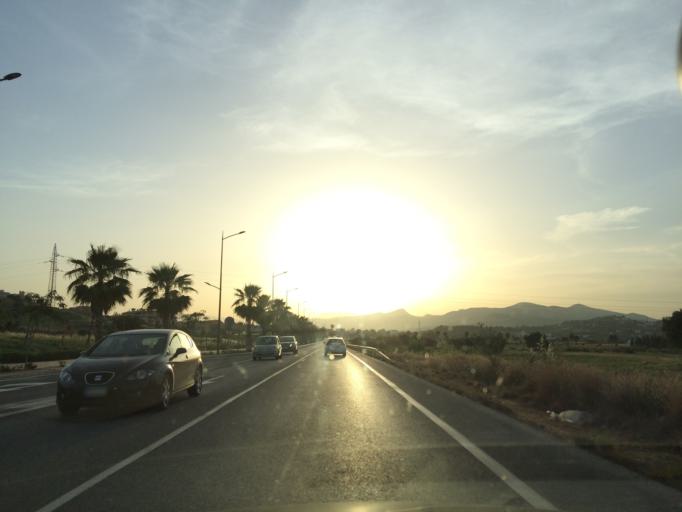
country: ES
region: Andalusia
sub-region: Provincia de Malaga
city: Alhaurin de la Torre
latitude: 36.6689
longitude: -4.5481
